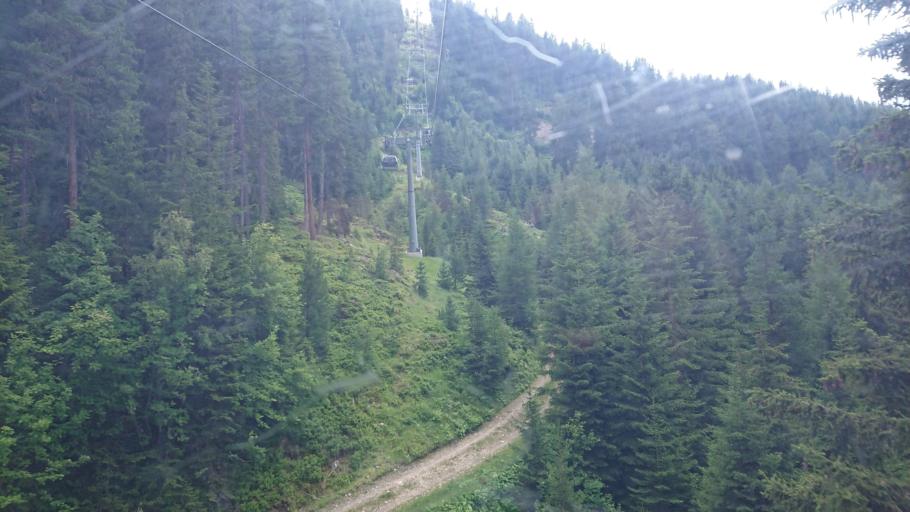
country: AT
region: Tyrol
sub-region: Politischer Bezirk Imst
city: Oetz
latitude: 47.2228
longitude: 10.9324
